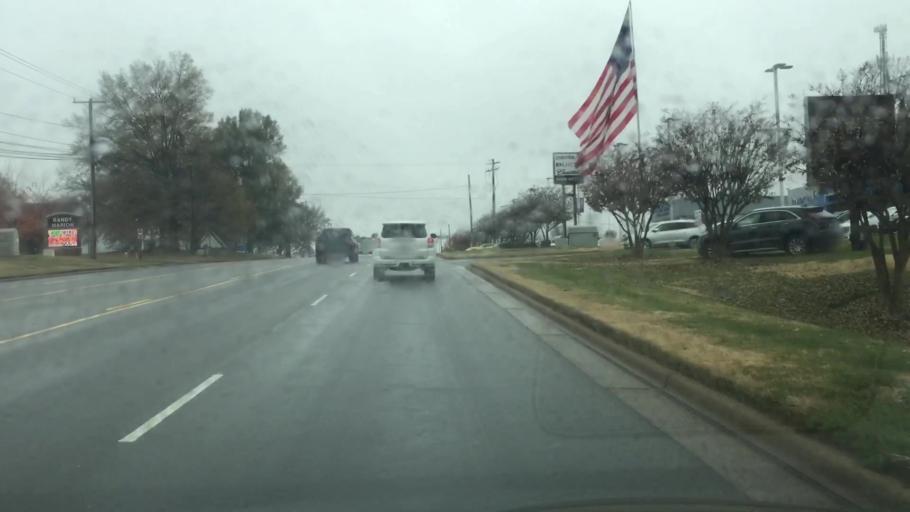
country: US
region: North Carolina
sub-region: Iredell County
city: Mooresville
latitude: 35.5908
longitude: -80.8453
